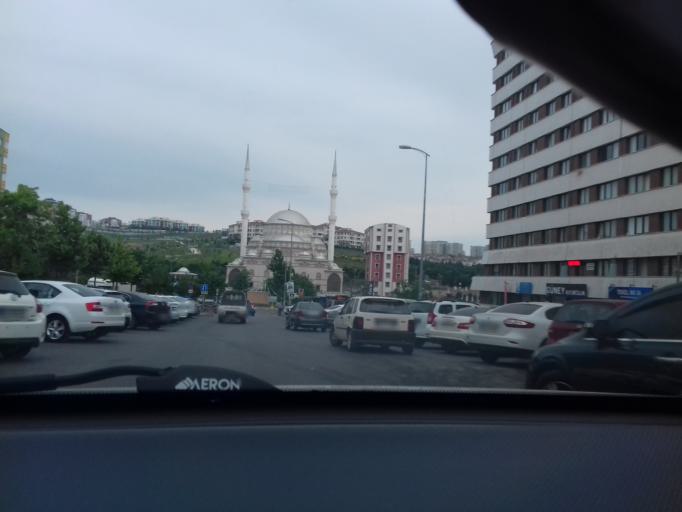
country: TR
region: Istanbul
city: Sultanbeyli
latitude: 40.9302
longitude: 29.3053
